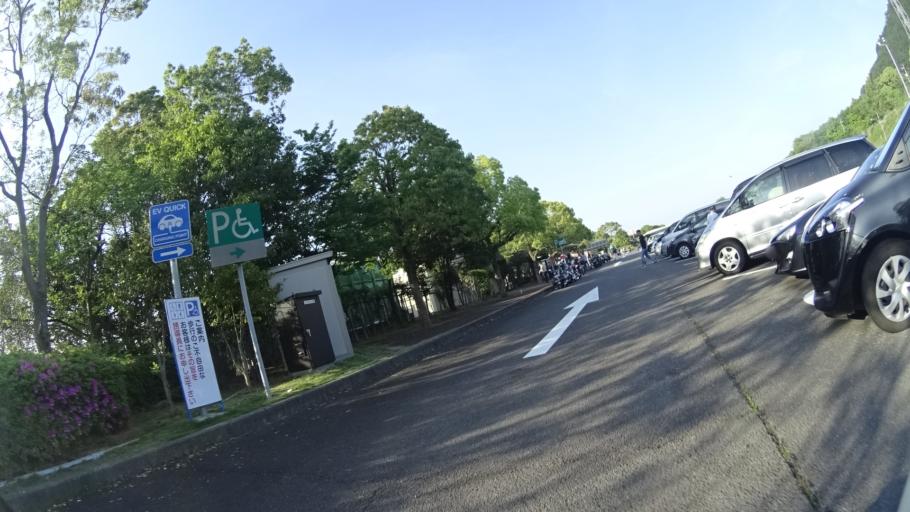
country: JP
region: Ehime
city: Kawanoecho
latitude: 34.0565
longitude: 133.6365
